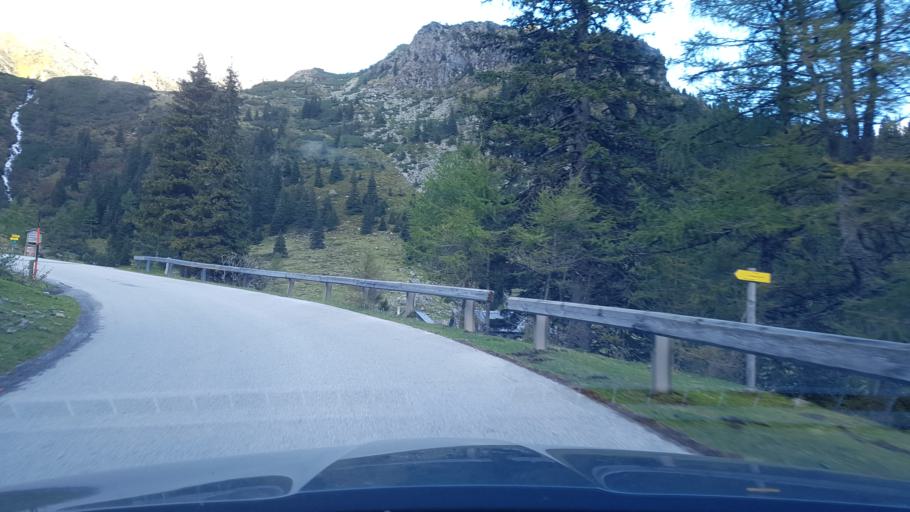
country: AT
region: Styria
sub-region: Politischer Bezirk Liezen
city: Sankt Nikolai im Solktal
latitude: 47.2789
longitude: 14.0811
